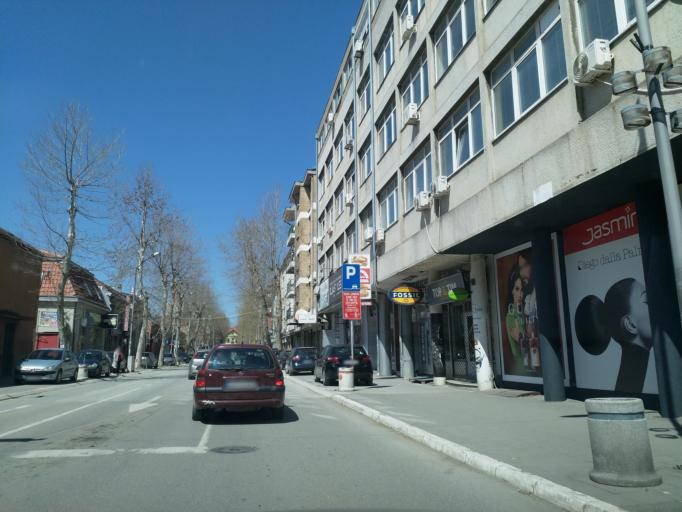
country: RS
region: Central Serbia
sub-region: Kolubarski Okrug
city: Valjevo
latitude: 44.2710
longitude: 19.8863
